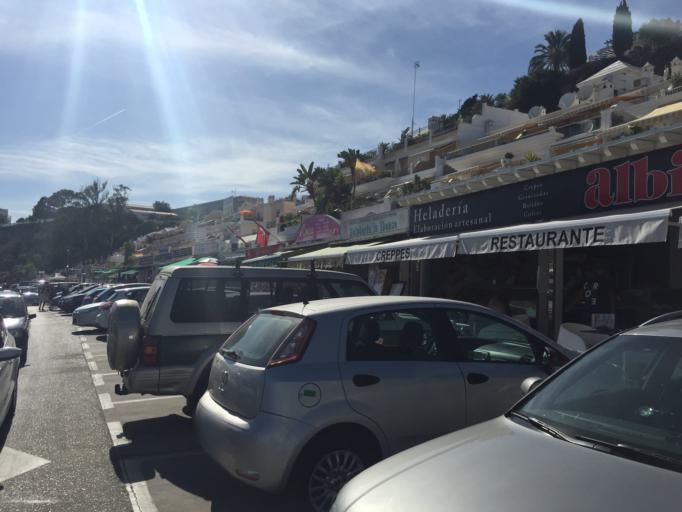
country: ES
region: Andalusia
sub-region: Provincia de Malaga
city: Nerja
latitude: 36.7510
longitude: -3.8671
